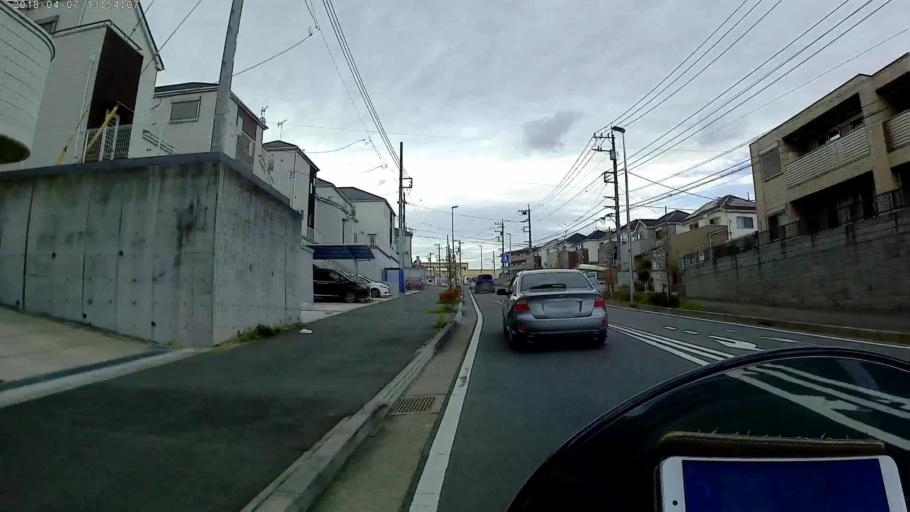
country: JP
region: Kanagawa
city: Isehara
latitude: 35.3675
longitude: 139.2868
